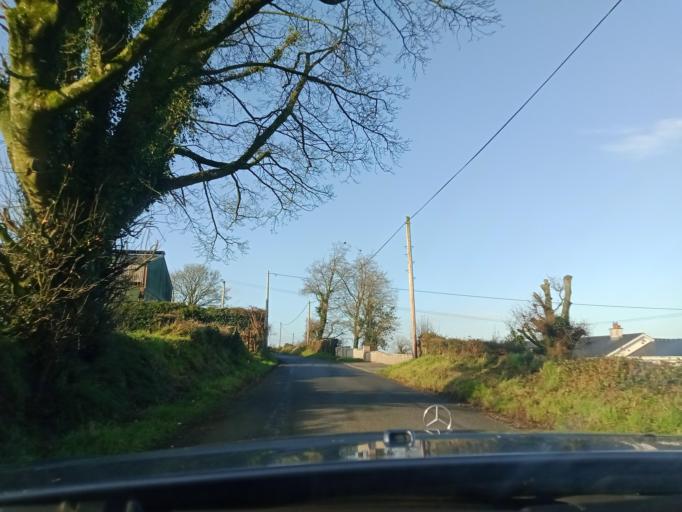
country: IE
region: Leinster
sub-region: Kilkenny
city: Callan
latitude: 52.4676
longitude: -7.4081
